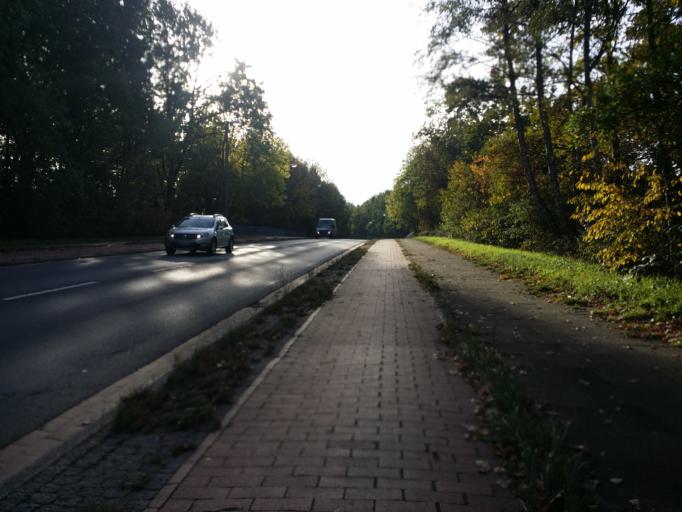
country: DE
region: Lower Saxony
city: Stuhr
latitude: 53.0415
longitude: 8.7258
